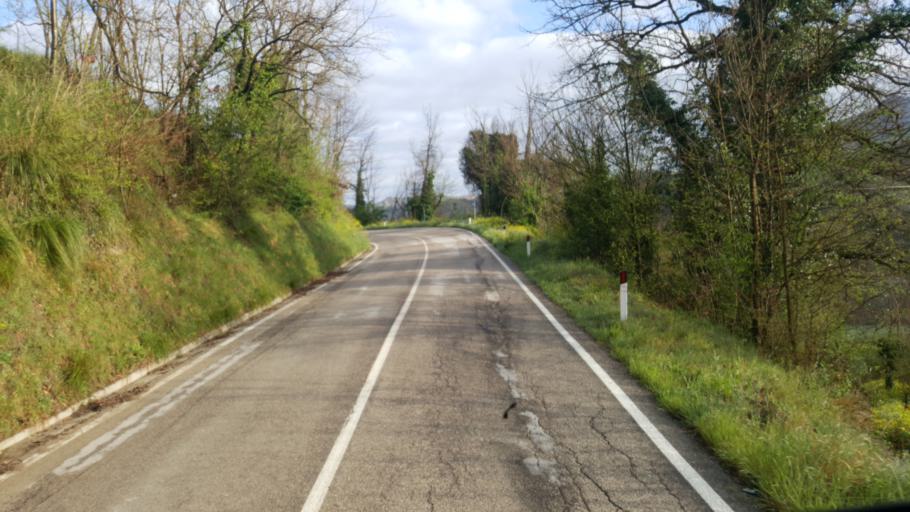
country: IT
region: The Marches
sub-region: Provincia di Ascoli Piceno
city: Venarotta
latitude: 42.8706
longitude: 13.5335
